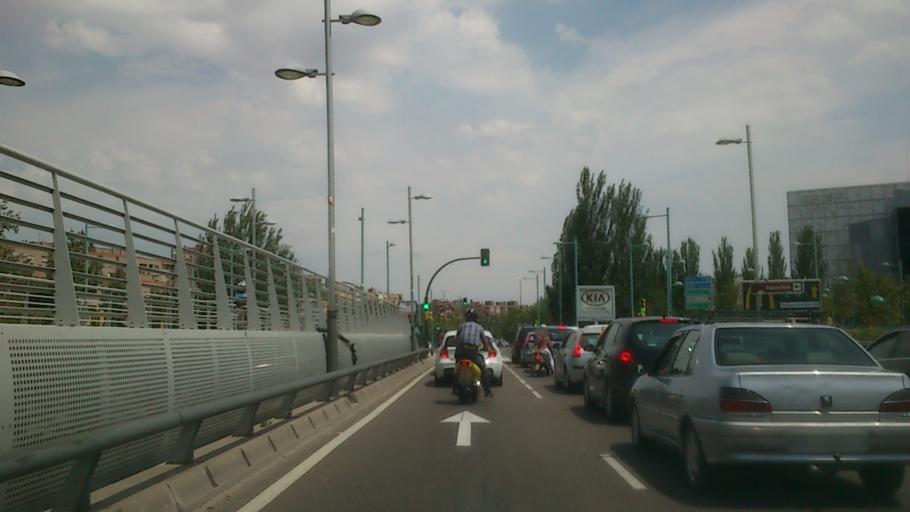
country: ES
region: Aragon
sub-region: Provincia de Zaragoza
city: Almozara
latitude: 41.6618
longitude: -0.8897
